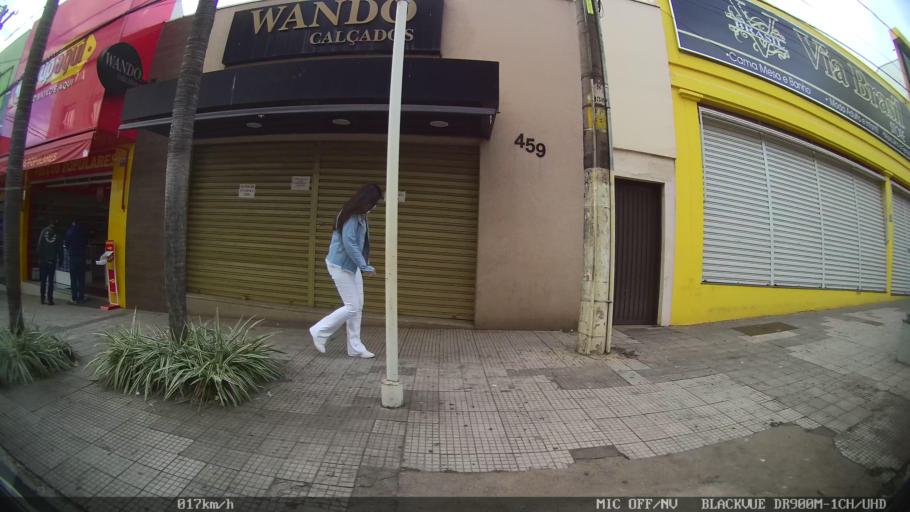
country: BR
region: Sao Paulo
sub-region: Catanduva
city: Catanduva
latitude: -21.1344
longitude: -48.9718
